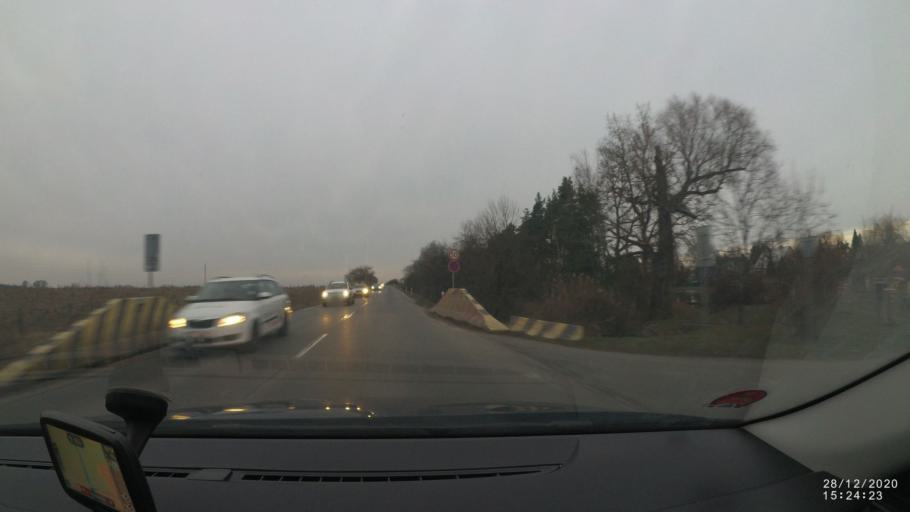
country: CZ
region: Praha
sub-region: Praha 20
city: Horni Pocernice
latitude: 50.0793
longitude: 14.6410
